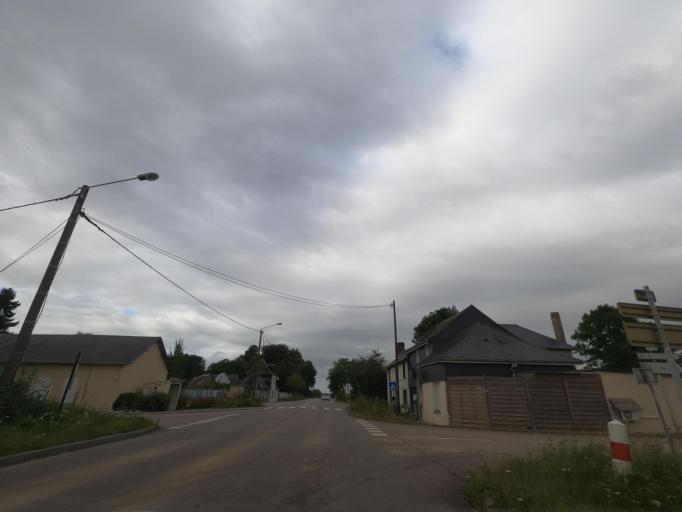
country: FR
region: Haute-Normandie
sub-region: Departement de l'Eure
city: Bourgtheroulde-Infreville
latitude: 49.2636
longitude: 0.8061
